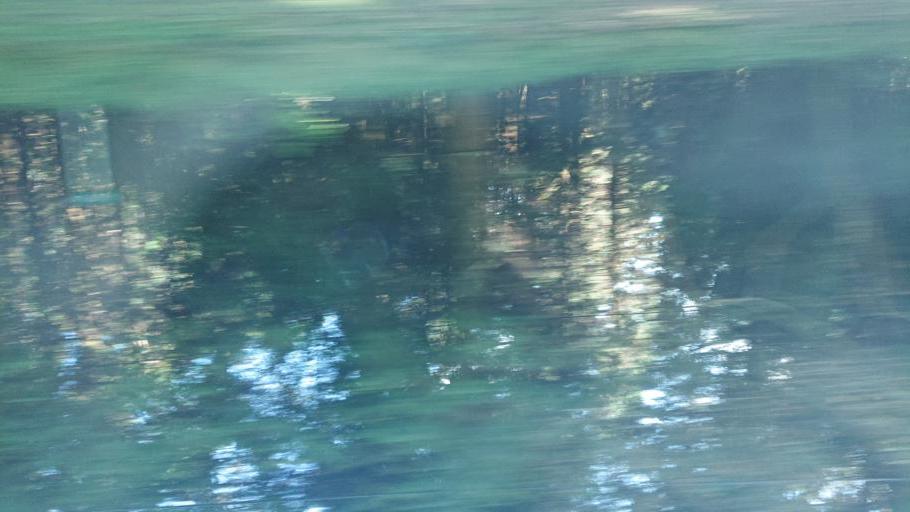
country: TW
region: Taiwan
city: Lugu
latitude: 23.5006
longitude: 120.8200
